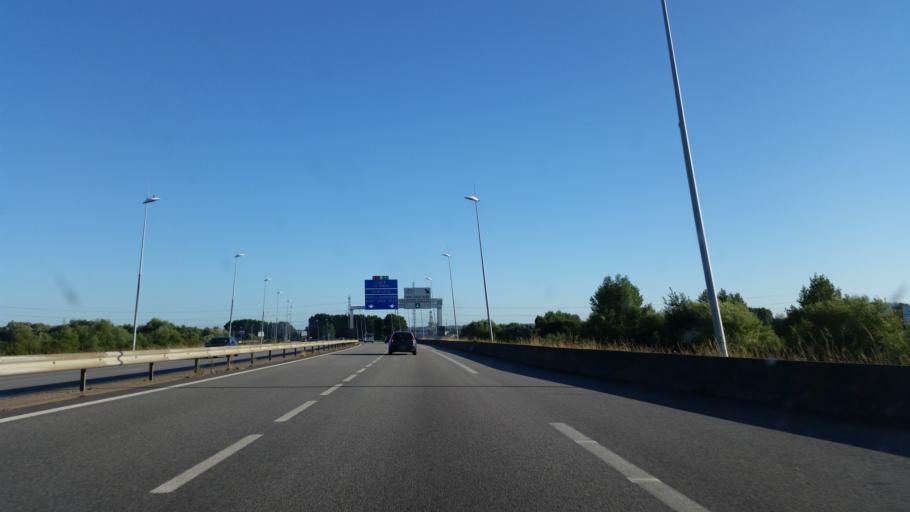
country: FR
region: Haute-Normandie
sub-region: Departement de la Seine-Maritime
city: Rogerville
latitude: 49.4855
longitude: 0.2631
